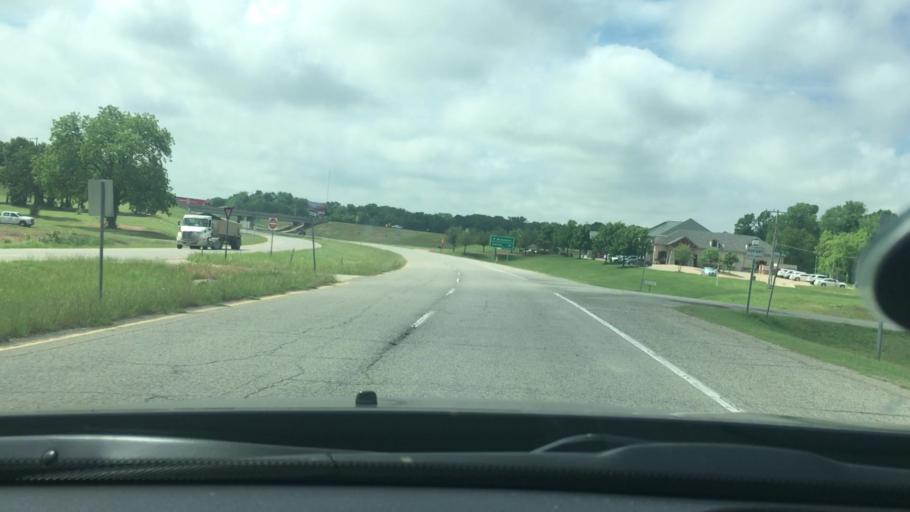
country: US
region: Oklahoma
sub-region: Bryan County
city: Durant
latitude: 34.0415
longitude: -96.3762
